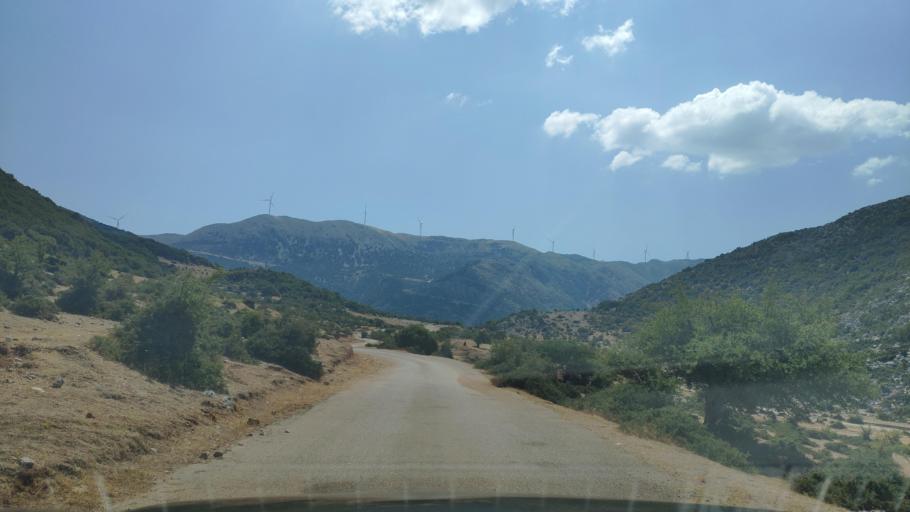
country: GR
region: West Greece
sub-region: Nomos Aitolias kai Akarnanias
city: Monastirakion
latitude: 38.7983
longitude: 20.9512
